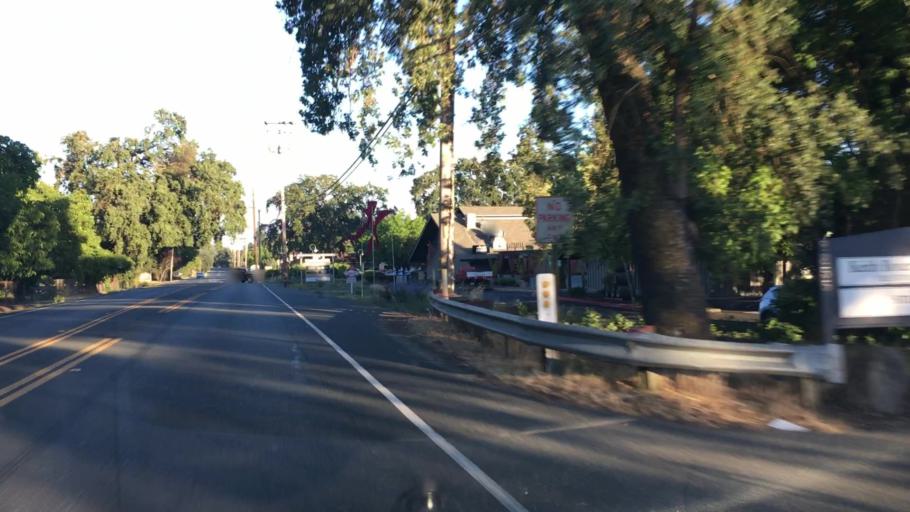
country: US
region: California
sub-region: Sonoma County
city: Kenwood
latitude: 38.4200
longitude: -122.5519
